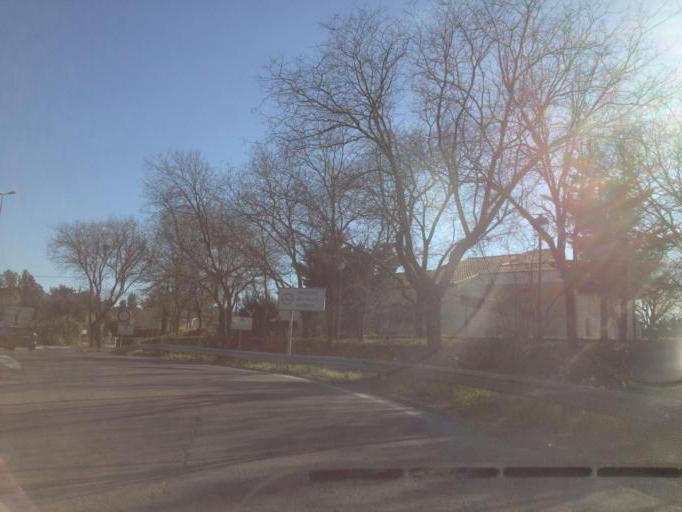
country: FR
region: Provence-Alpes-Cote d'Azur
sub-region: Departement des Bouches-du-Rhone
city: Bouc-Bel-Air
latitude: 43.5037
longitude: 5.3932
